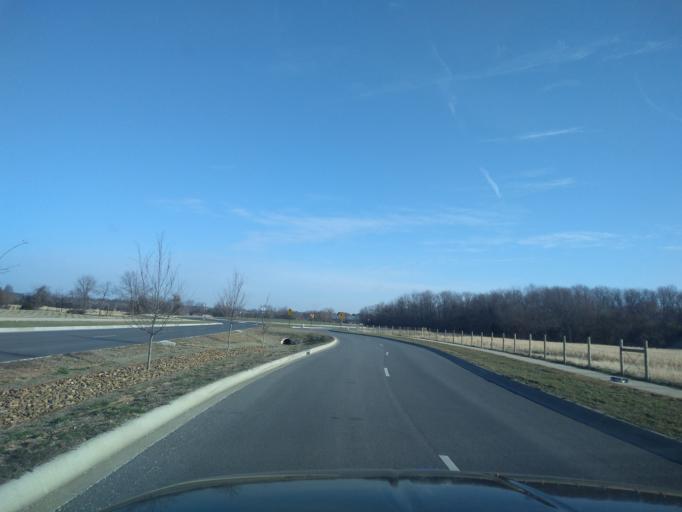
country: US
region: Arkansas
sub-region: Washington County
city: Farmington
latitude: 36.0629
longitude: -94.2202
